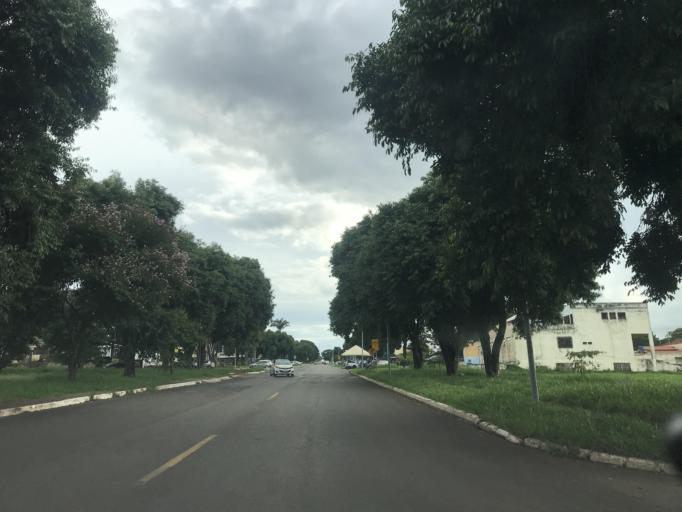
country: BR
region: Federal District
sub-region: Brasilia
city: Brasilia
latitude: -15.6411
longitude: -47.7925
